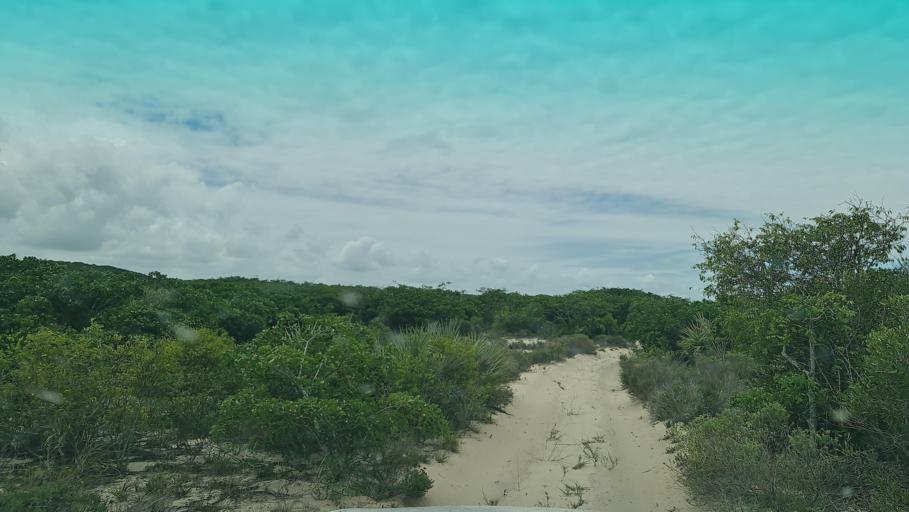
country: MZ
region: Maputo
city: Manhica
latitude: -25.6382
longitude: 32.7832
